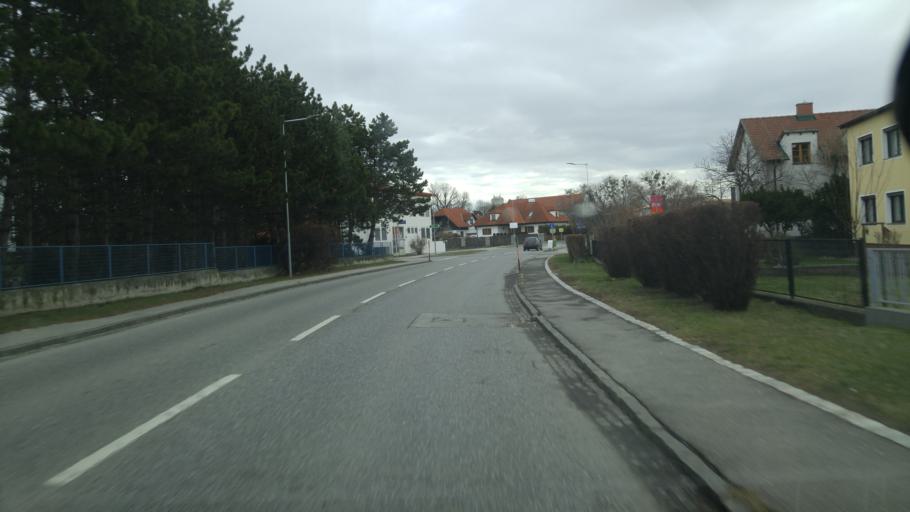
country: AT
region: Lower Austria
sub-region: Politischer Bezirk Wien-Umgebung
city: Himberg
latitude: 48.0873
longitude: 16.4339
